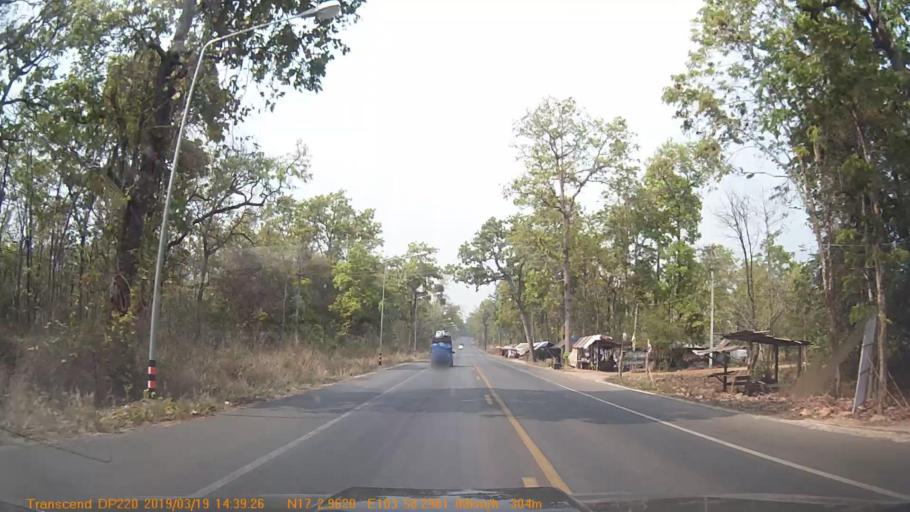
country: TH
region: Sakon Nakhon
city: Phu Phan
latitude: 17.0497
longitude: 103.9716
